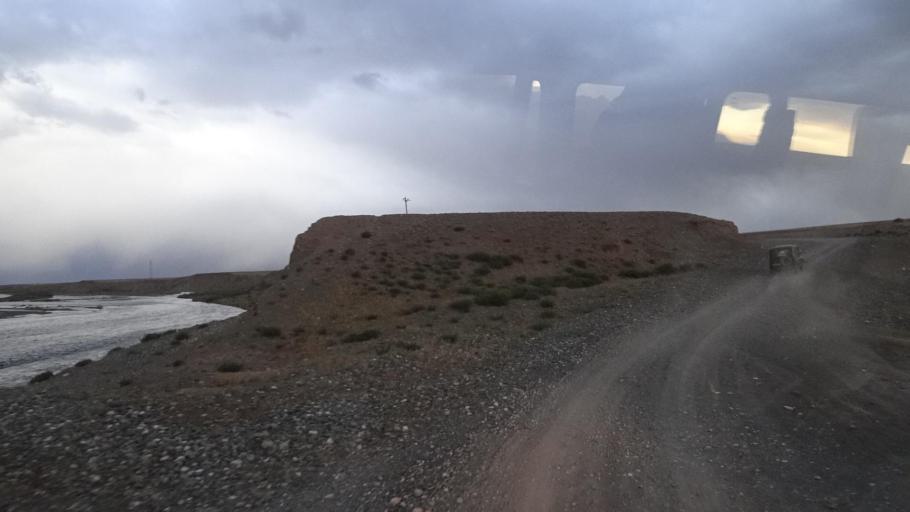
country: KG
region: Osh
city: Osh
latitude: 39.6572
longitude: 72.8770
